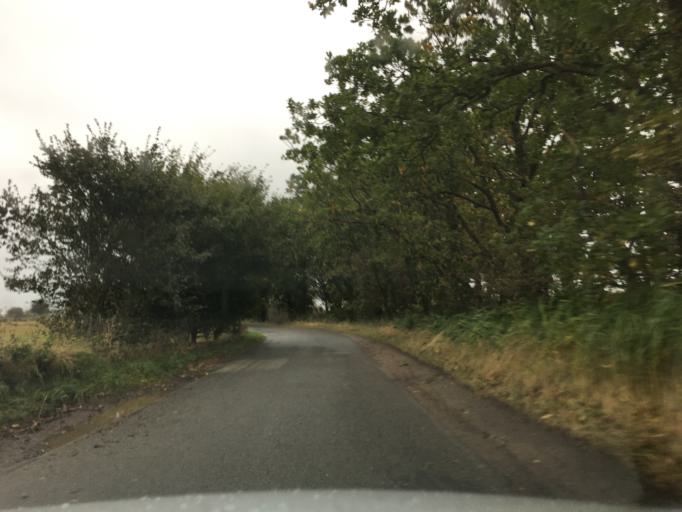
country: DE
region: Schleswig-Holstein
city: Strande
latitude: 54.4485
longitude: 10.1897
